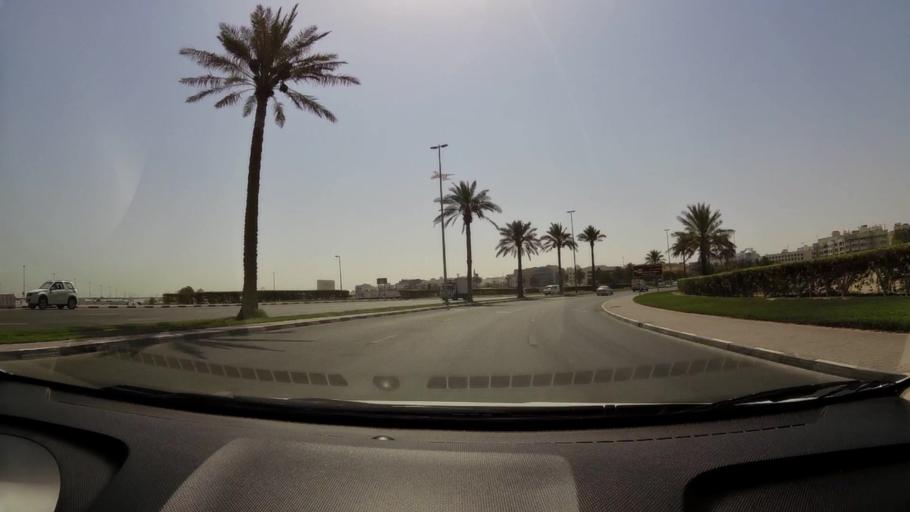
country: AE
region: Ash Shariqah
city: Sharjah
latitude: 25.2813
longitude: 55.3088
